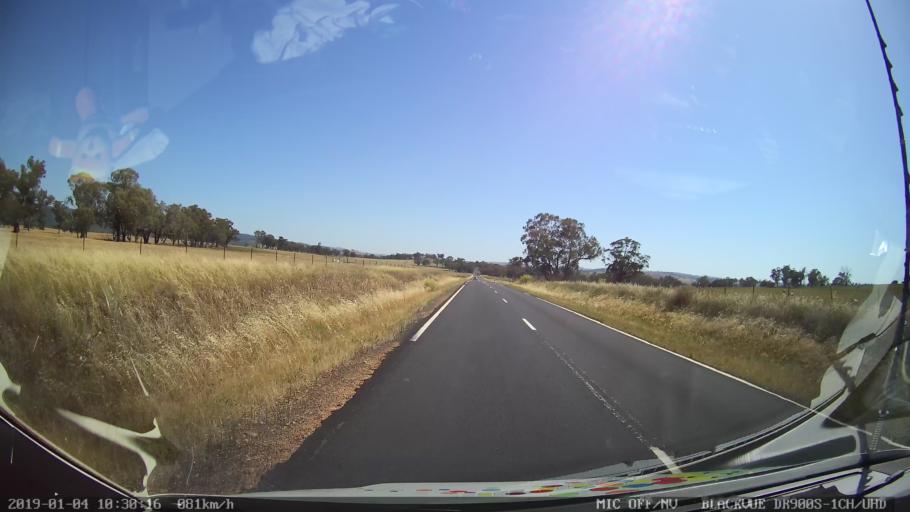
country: AU
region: New South Wales
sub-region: Cabonne
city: Canowindra
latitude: -33.3478
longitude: 148.6268
